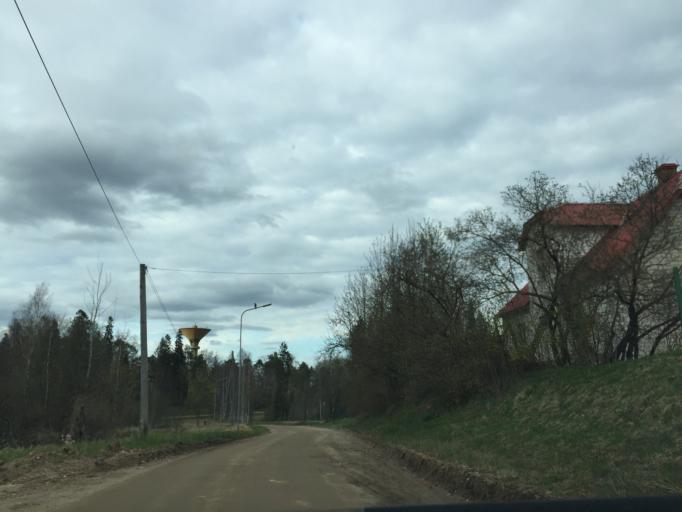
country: LV
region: Aluksnes Rajons
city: Aluksne
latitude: 57.4189
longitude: 27.0375
